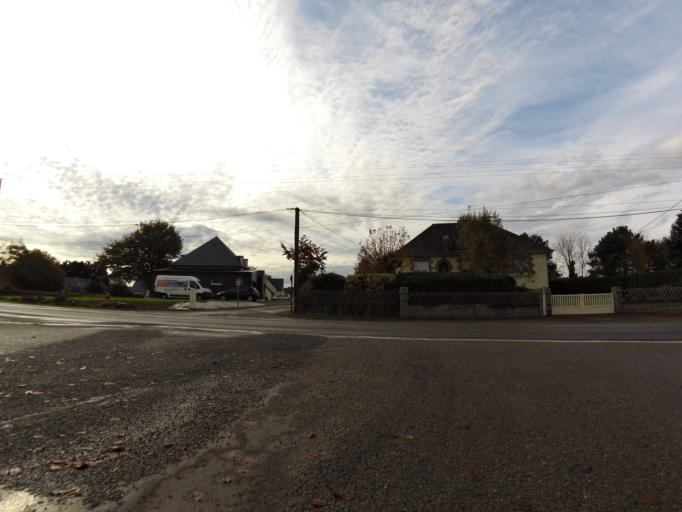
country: FR
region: Brittany
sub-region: Departement d'Ille-et-Vilaine
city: Bourg-des-Comptes
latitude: 47.9315
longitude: -1.7569
